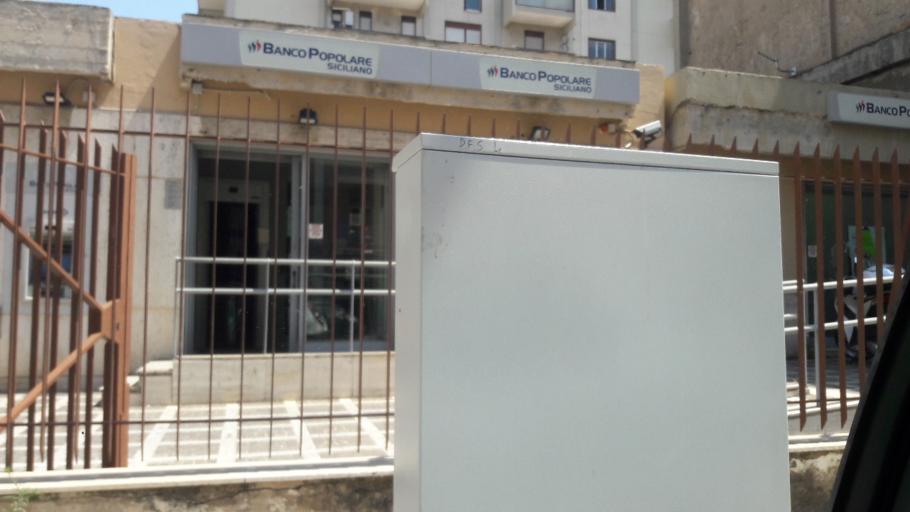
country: IT
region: Sicily
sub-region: Palermo
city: Ciaculli
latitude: 38.0996
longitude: 13.3729
